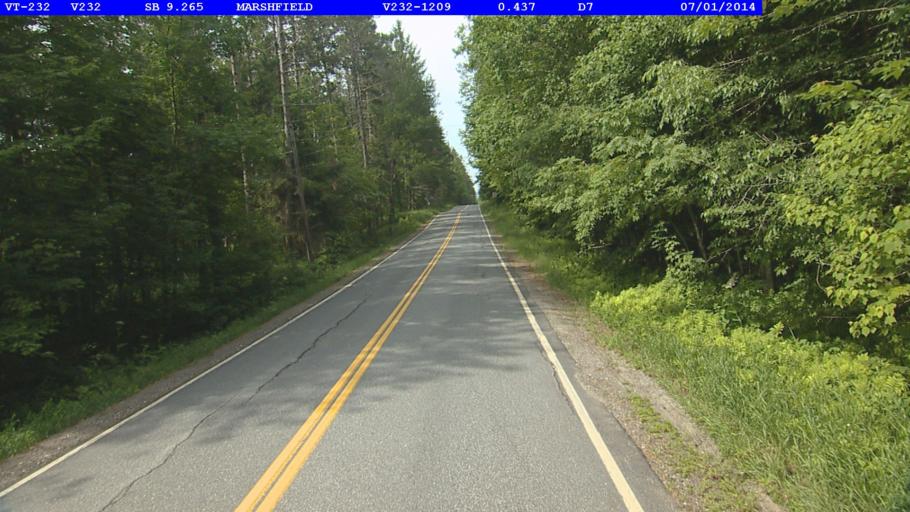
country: US
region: Vermont
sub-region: Caledonia County
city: Hardwick
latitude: 44.3223
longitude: -72.2900
